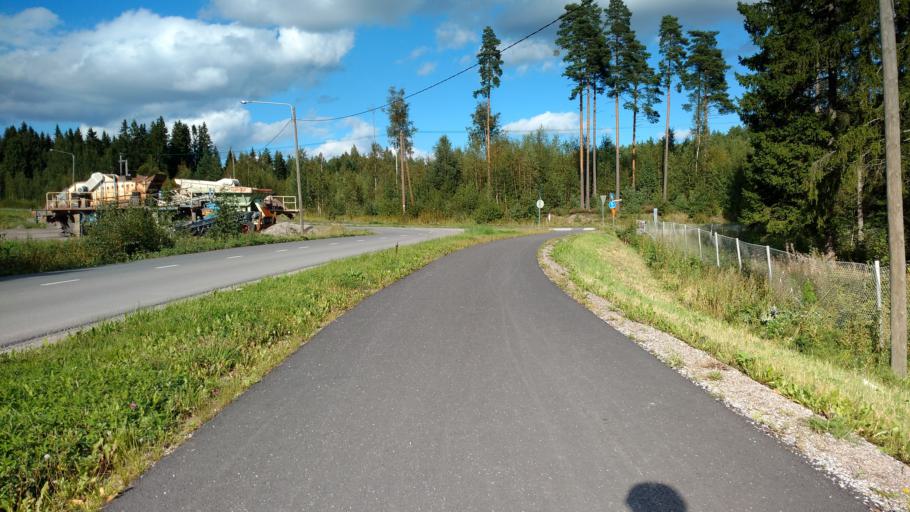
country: FI
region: Varsinais-Suomi
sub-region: Salo
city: Salo
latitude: 60.3801
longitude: 23.1906
